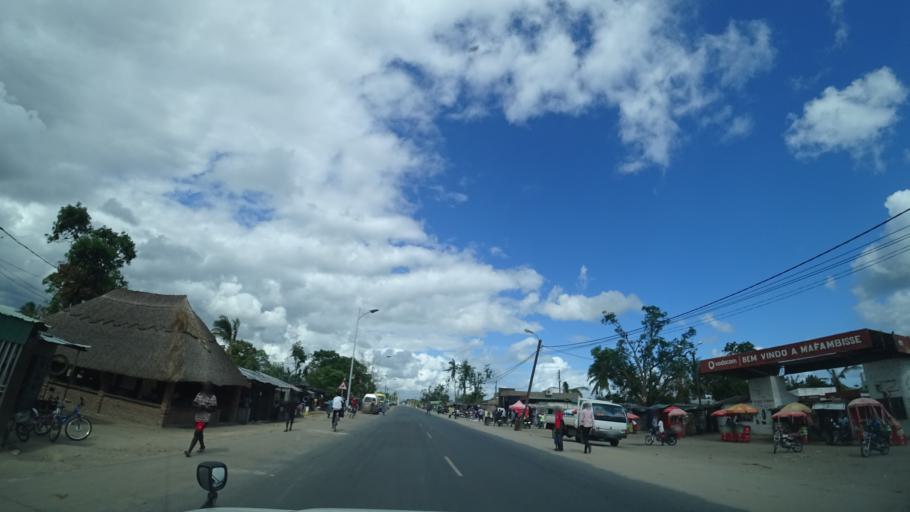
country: MZ
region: Sofala
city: Dondo
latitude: -19.5364
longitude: 34.6335
